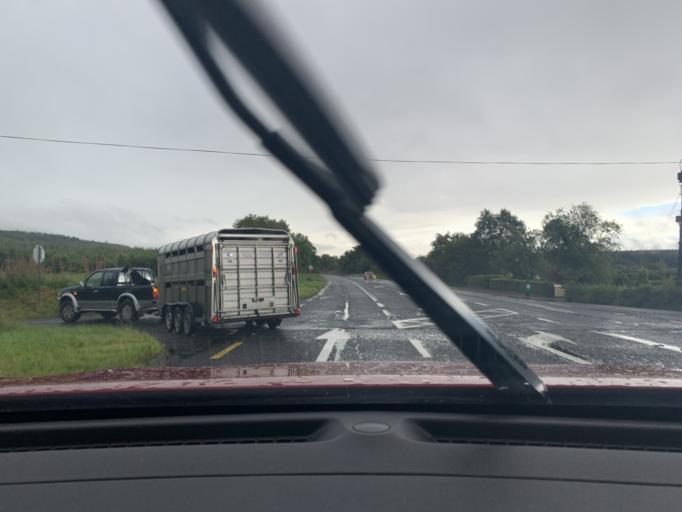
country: IE
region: Ulster
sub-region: County Donegal
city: Ballybofey
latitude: 54.8453
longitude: -7.7514
